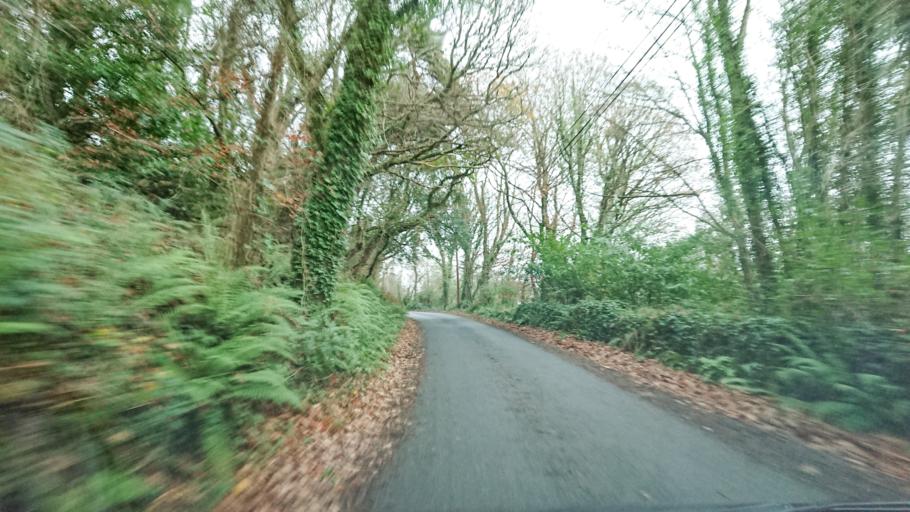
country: IE
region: Munster
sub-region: Waterford
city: Dunmore East
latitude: 52.2059
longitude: -7.0013
